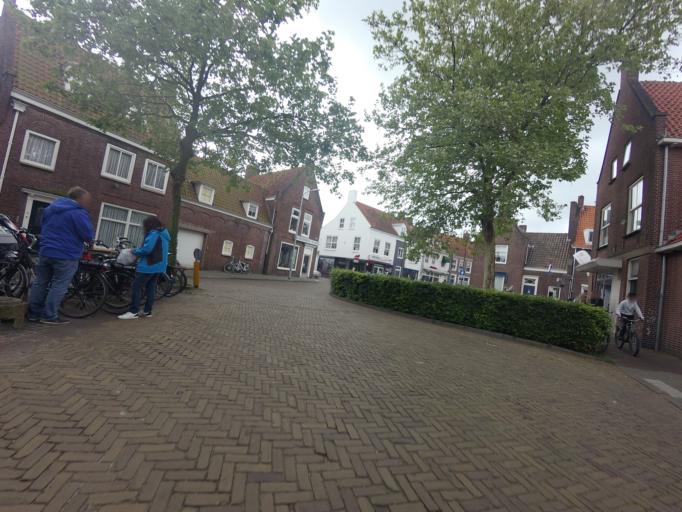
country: NL
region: Zeeland
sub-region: Gemeente Middelburg
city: Middelburg
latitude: 51.4973
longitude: 3.6123
